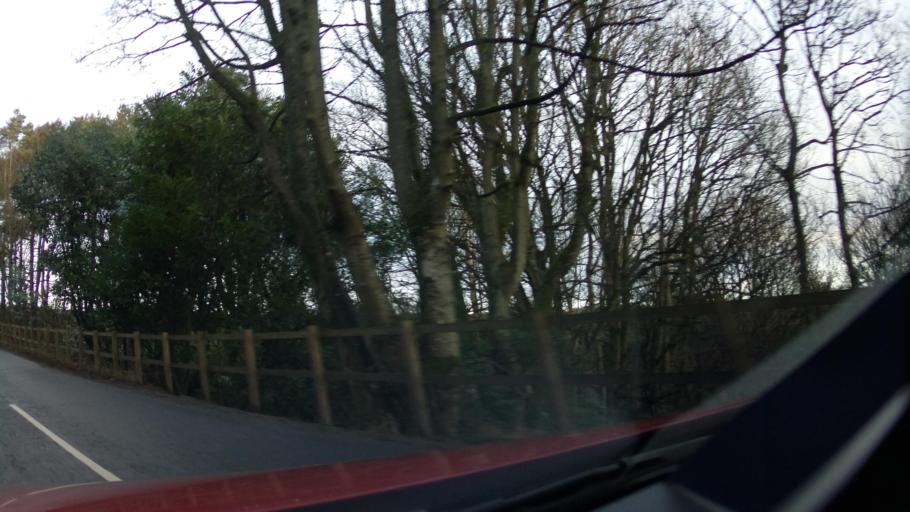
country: GB
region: Scotland
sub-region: Fife
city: Tayport
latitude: 56.5228
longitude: -2.8121
